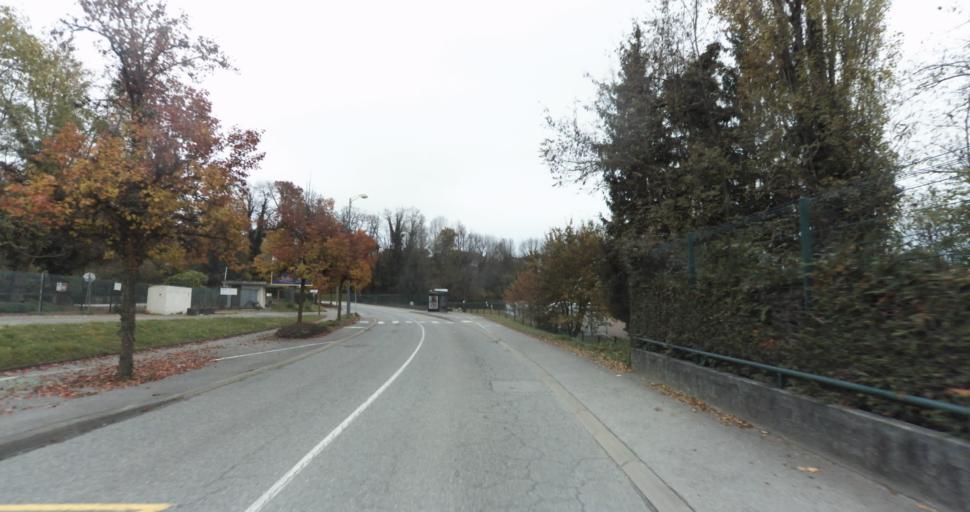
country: FR
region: Rhone-Alpes
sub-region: Departement de la Haute-Savoie
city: Cran-Gevrier
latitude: 45.9116
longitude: 6.1081
